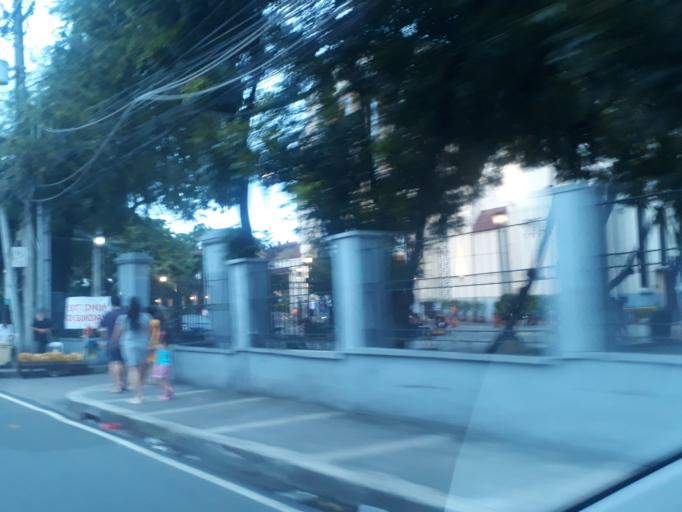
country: PH
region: Calabarzon
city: Del Monte
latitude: 14.6266
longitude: 121.0111
